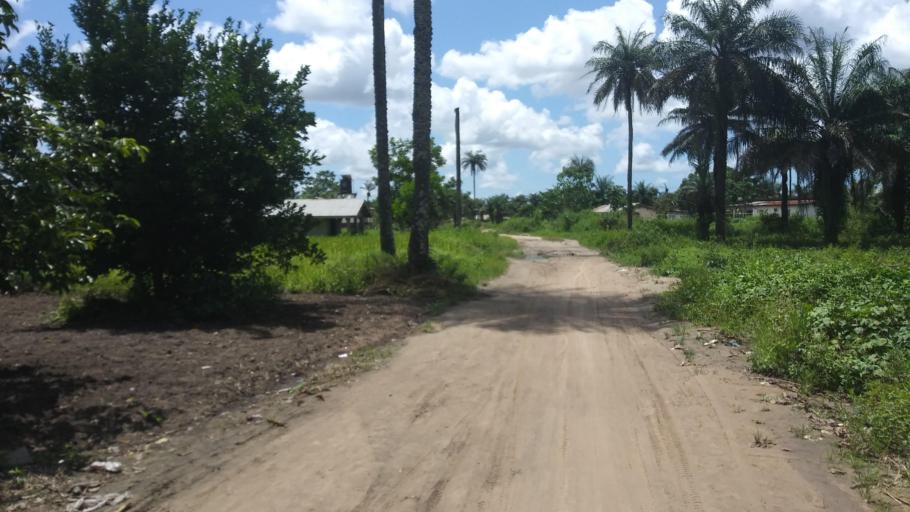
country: SL
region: Northern Province
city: Makeni
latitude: 8.8757
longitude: -11.9945
